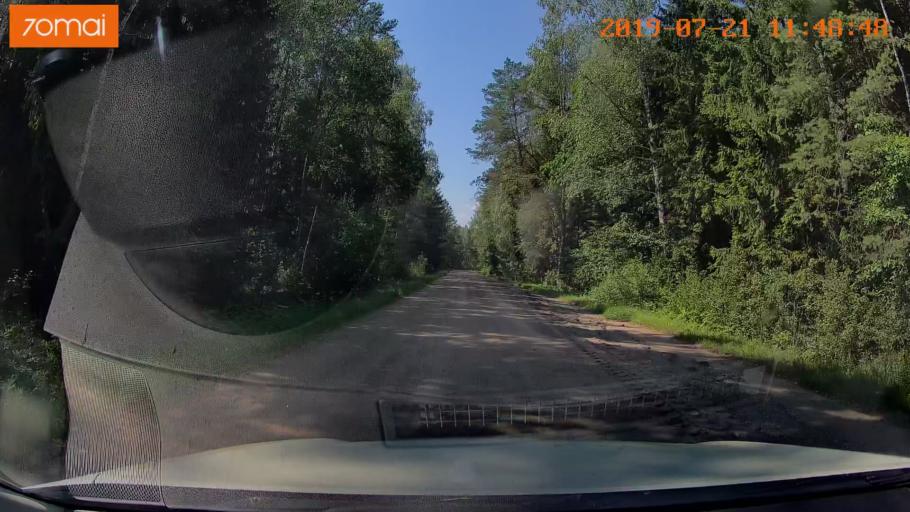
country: BY
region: Grodnenskaya
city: Lyubcha
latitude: 53.8957
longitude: 26.0457
